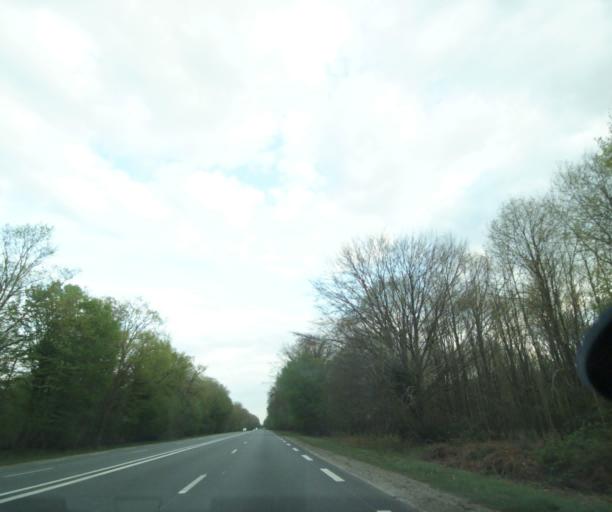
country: FR
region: Ile-de-France
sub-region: Departement de Seine-et-Marne
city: Fontainebleau
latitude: 48.4247
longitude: 2.6668
